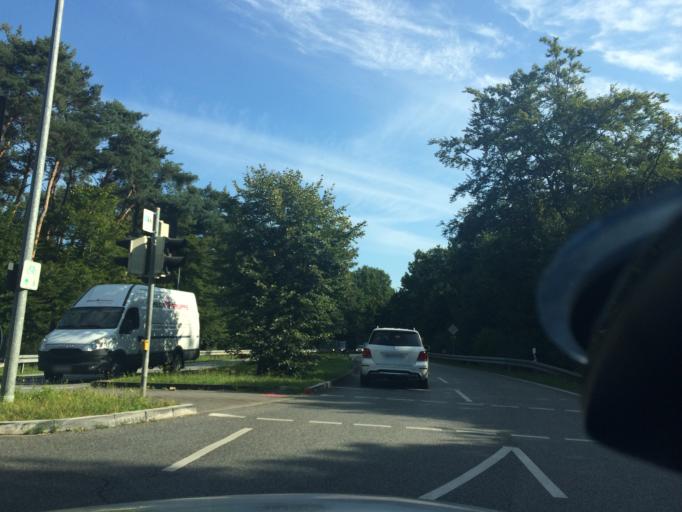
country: DE
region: Hesse
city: Morfelden-Walldorf
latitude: 50.0113
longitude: 8.5991
